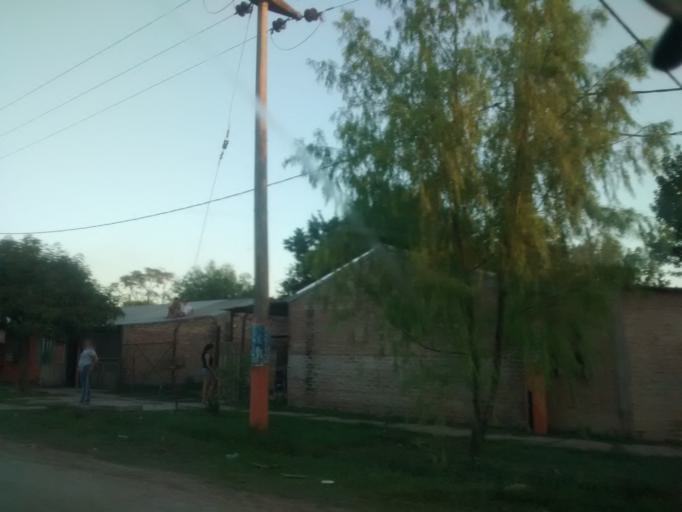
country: AR
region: Chaco
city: Fontana
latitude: -27.3982
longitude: -58.9913
